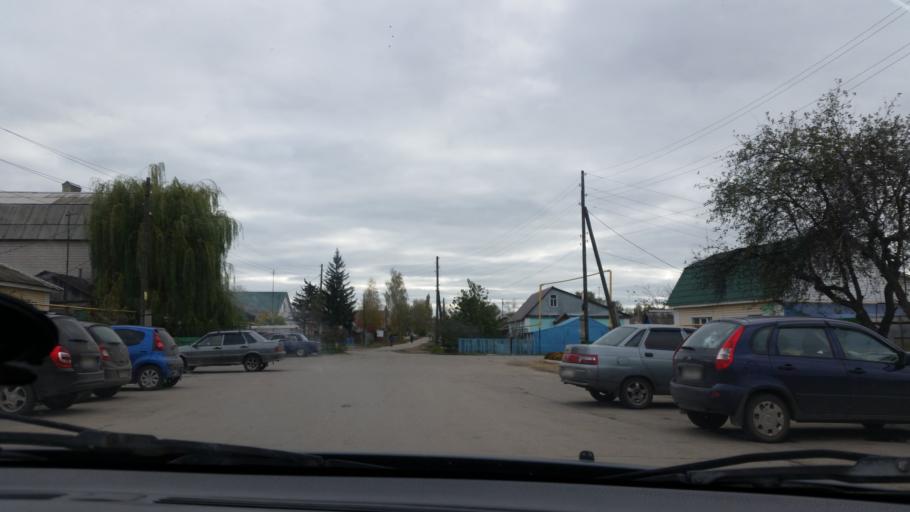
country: RU
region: Lipetsk
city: Gryazi
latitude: 52.4902
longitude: 39.9505
